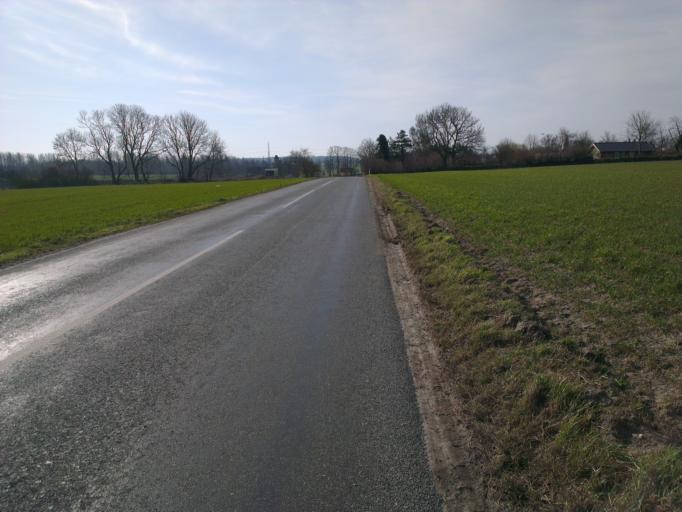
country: DK
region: Capital Region
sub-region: Frederikssund Kommune
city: Jaegerspris
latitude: 55.8147
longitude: 11.9522
